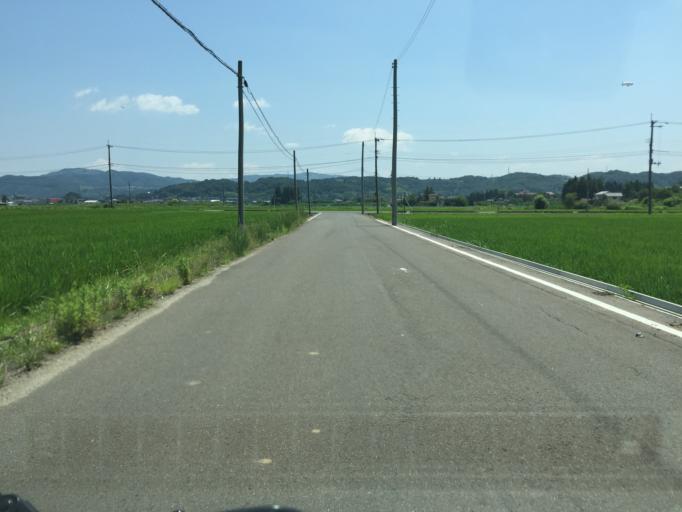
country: JP
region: Fukushima
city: Fukushima-shi
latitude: 37.7171
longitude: 140.4371
